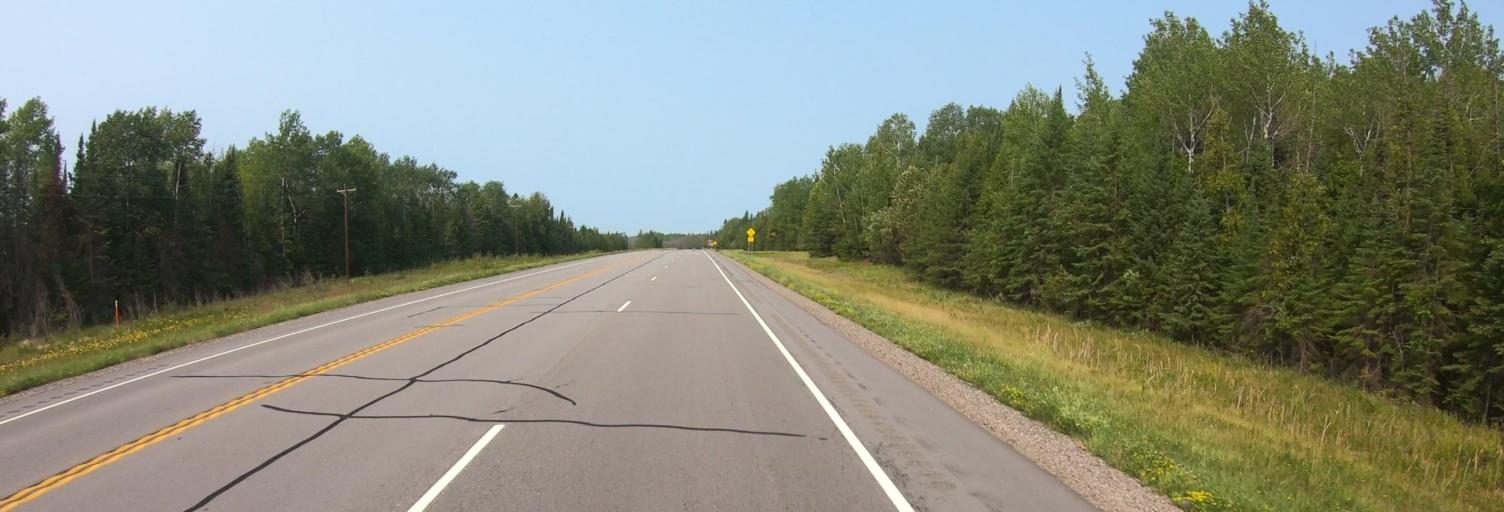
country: CA
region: Ontario
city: Fort Frances
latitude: 48.4059
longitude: -93.0363
